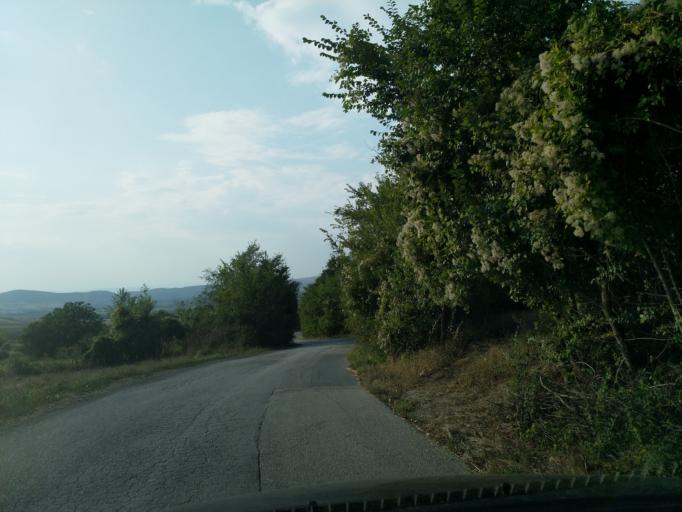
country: RS
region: Central Serbia
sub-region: Pomoravski Okrug
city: Paracin
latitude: 43.8440
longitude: 21.5287
